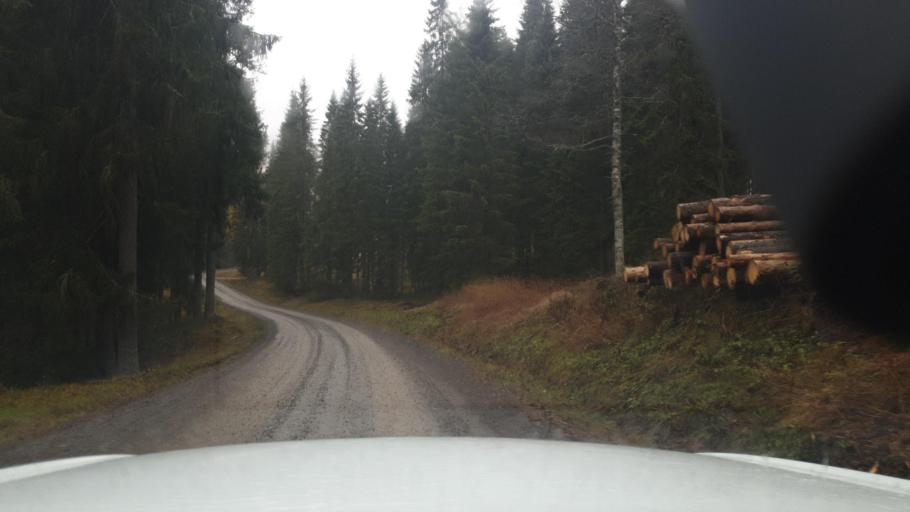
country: SE
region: Vaermland
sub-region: Sunne Kommun
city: Sunne
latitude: 59.8568
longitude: 12.8894
